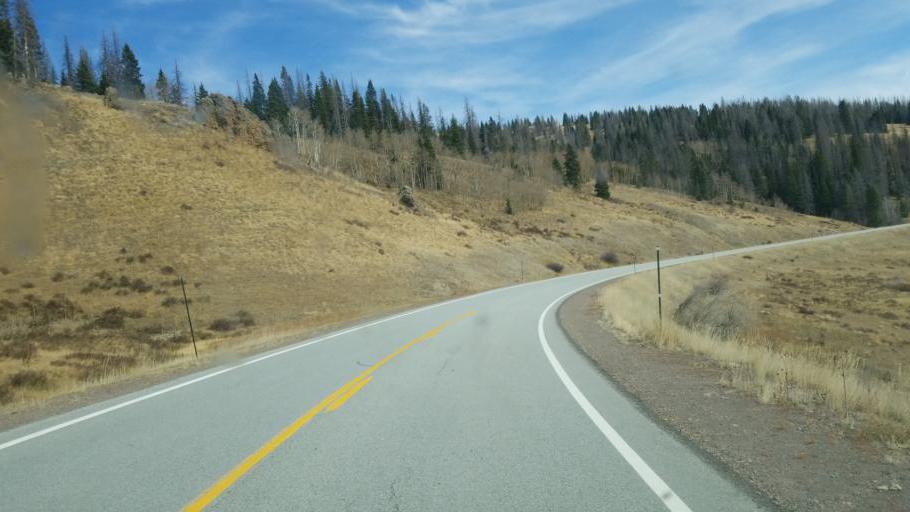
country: US
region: New Mexico
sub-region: Rio Arriba County
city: Chama
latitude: 37.0219
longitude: -106.4459
